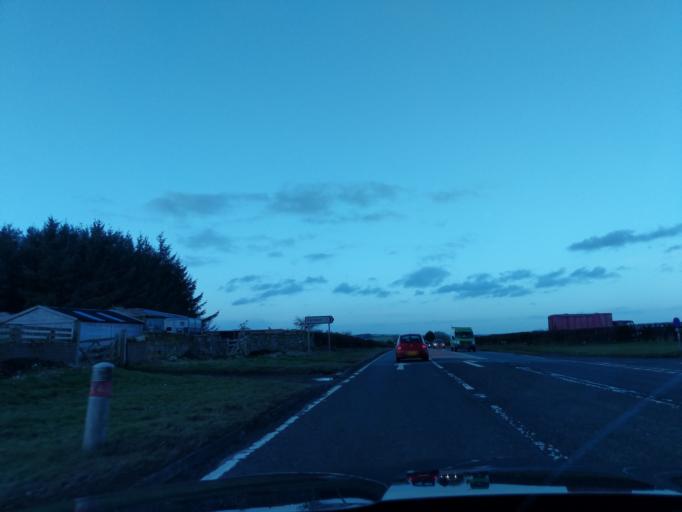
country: GB
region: England
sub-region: Northumberland
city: Felton
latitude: 55.2366
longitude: -1.7042
